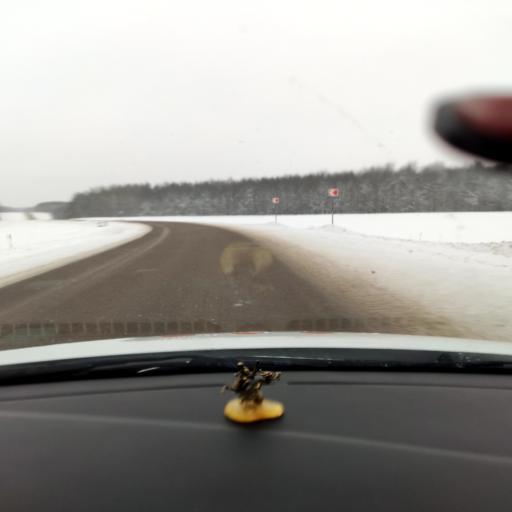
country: RU
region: Tatarstan
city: Vysokaya Gora
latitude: 56.0911
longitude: 49.1797
